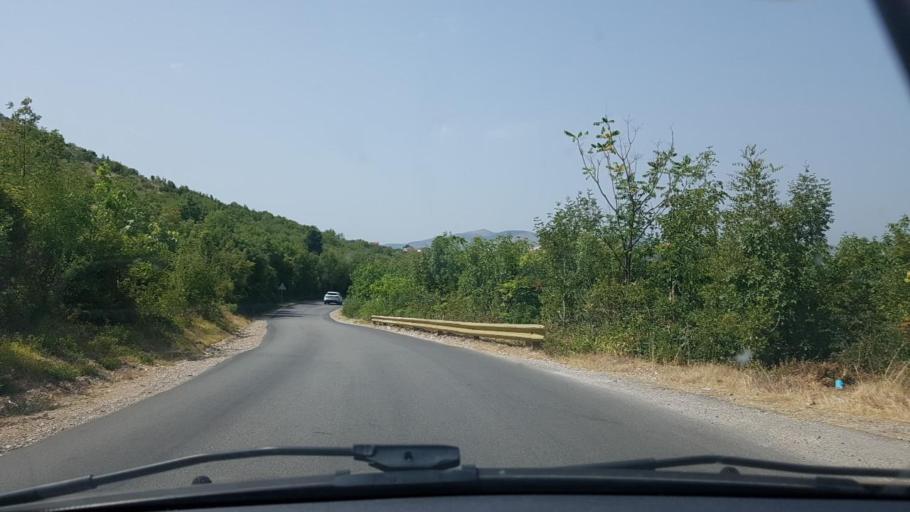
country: HR
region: Dubrovacko-Neretvanska
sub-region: Grad Dubrovnik
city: Metkovic
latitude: 43.0435
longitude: 17.7084
